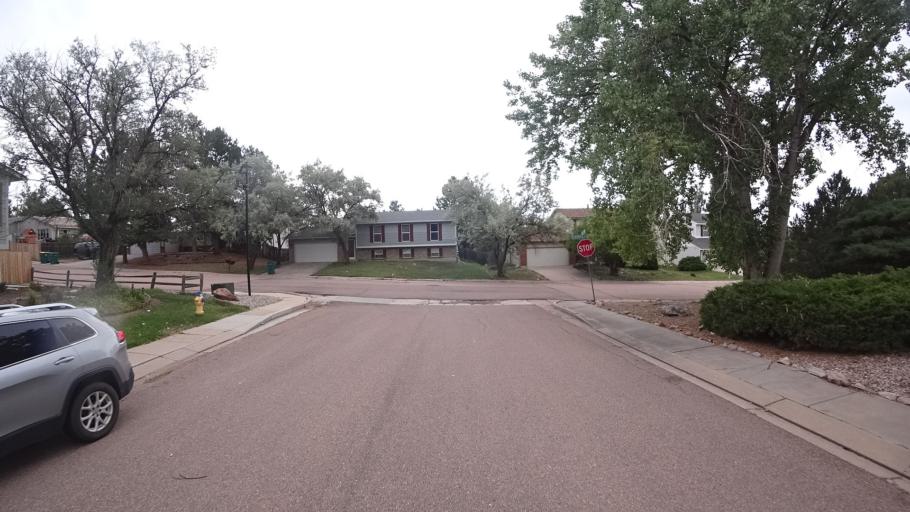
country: US
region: Colorado
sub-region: El Paso County
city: Air Force Academy
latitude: 38.9240
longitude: -104.8344
